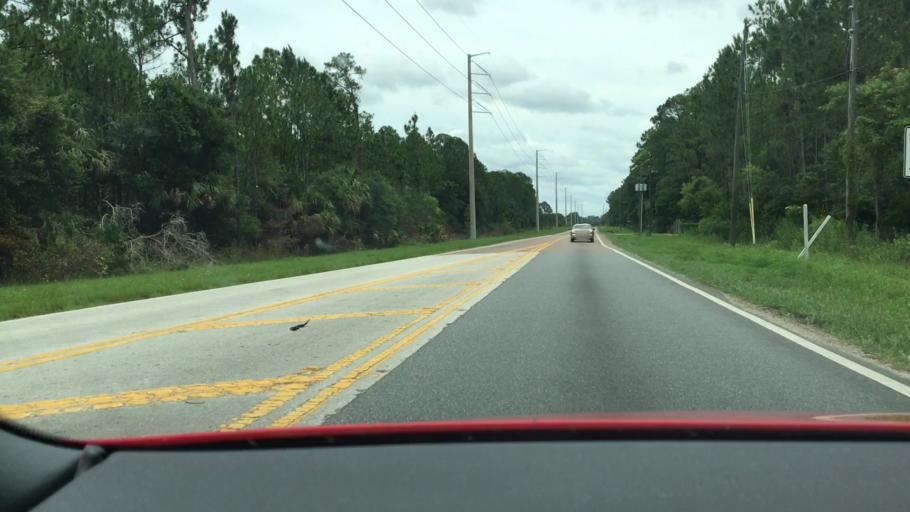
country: US
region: Florida
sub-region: Lake County
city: Eustis
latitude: 28.8753
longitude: -81.6846
